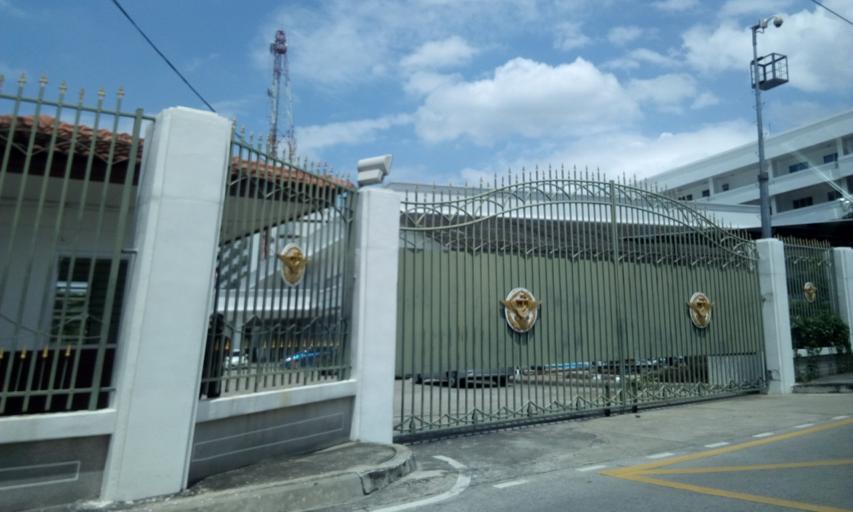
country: TH
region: Bangkok
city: Lak Si
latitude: 13.8861
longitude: 100.5632
